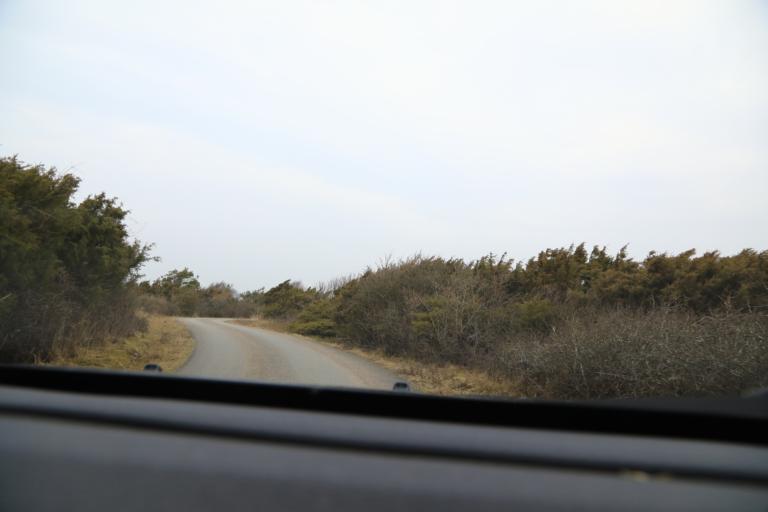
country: SE
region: Halland
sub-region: Kungsbacka Kommun
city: Frillesas
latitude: 57.2663
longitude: 12.1098
